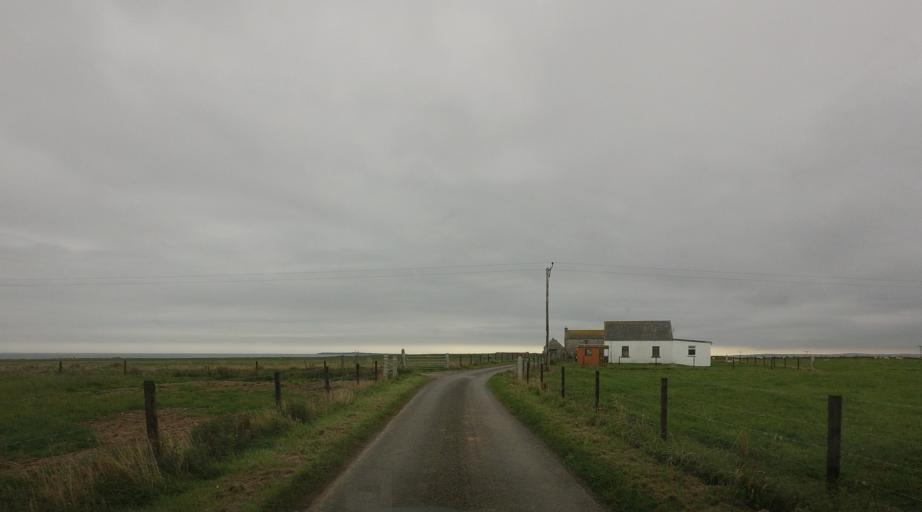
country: GB
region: Scotland
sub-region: Orkney Islands
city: Orkney
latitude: 58.7352
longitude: -2.9586
